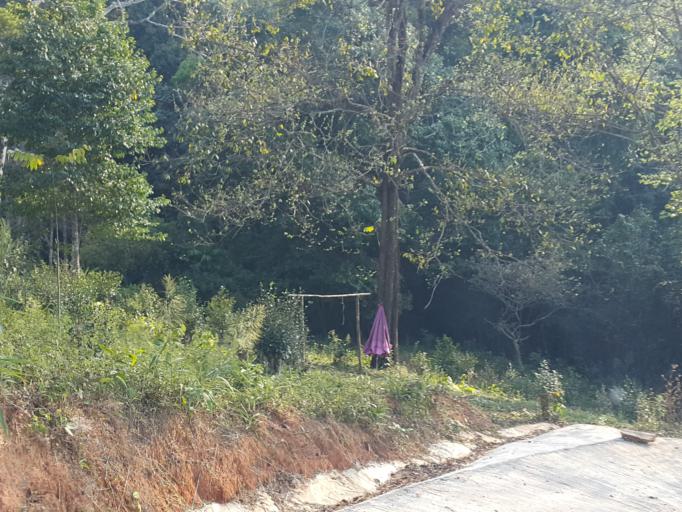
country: TH
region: Chiang Mai
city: Samoeng
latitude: 19.0154
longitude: 98.7636
